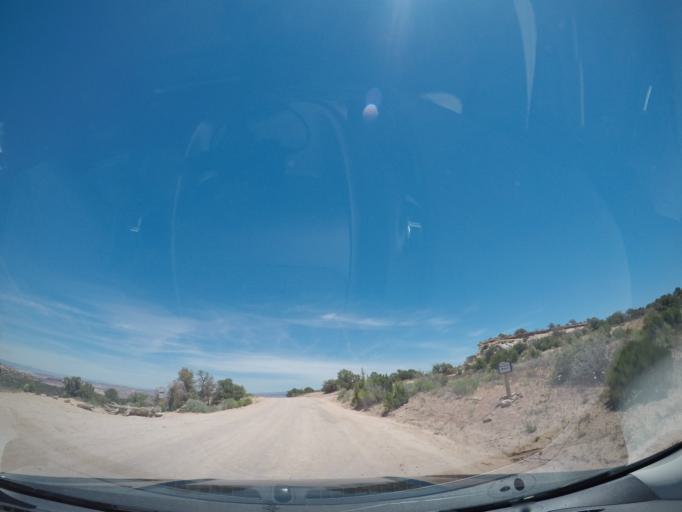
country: US
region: Utah
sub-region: Grand County
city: Moab
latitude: 38.5734
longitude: -109.7919
